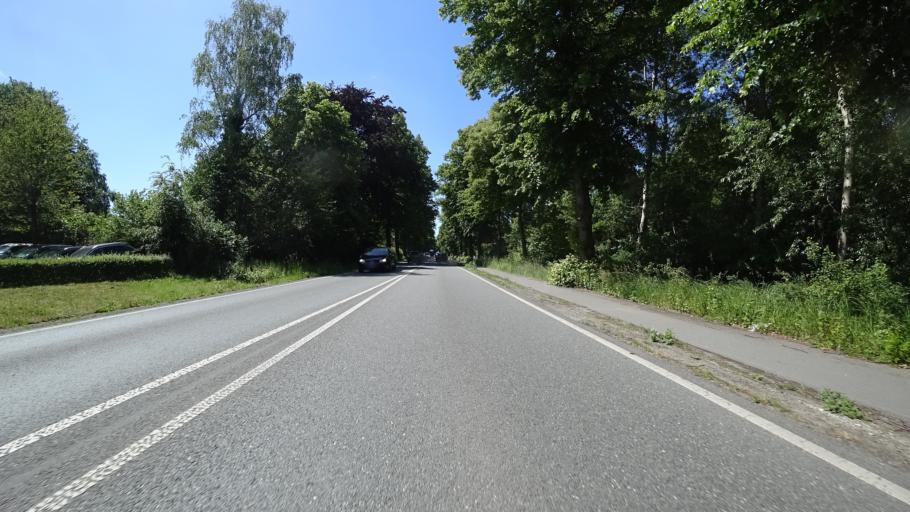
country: DE
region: North Rhine-Westphalia
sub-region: Regierungsbezirk Detmold
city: Guetersloh
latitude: 51.9263
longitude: 8.4056
